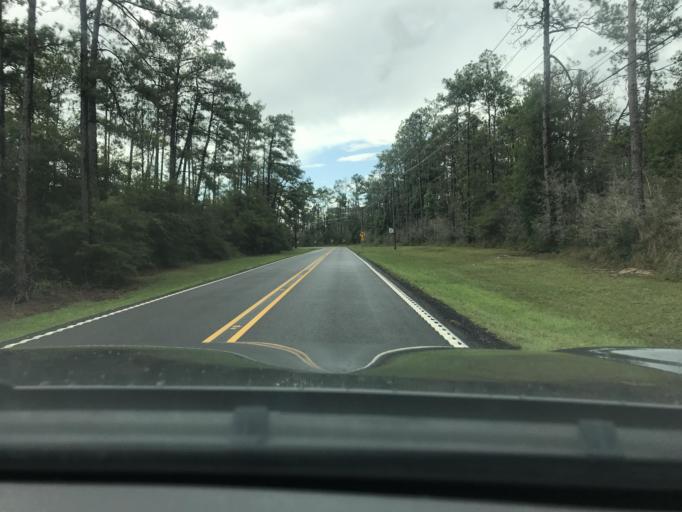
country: US
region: Louisiana
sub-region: Calcasieu Parish
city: Westlake
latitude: 30.3034
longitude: -93.2585
